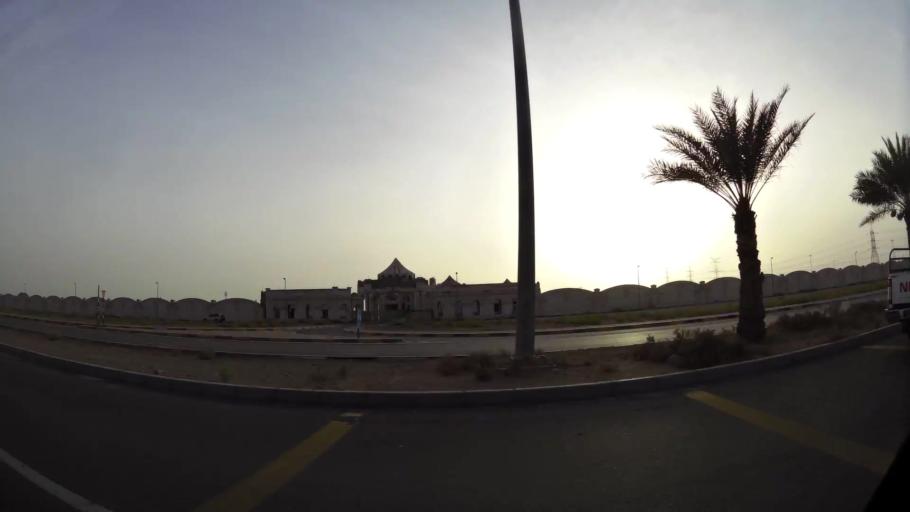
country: OM
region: Al Buraimi
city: Al Buraymi
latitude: 24.2717
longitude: 55.7206
